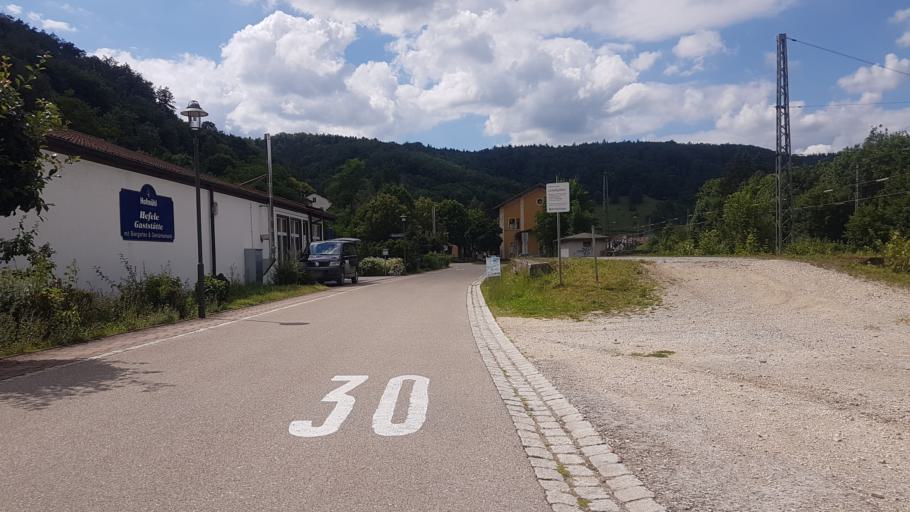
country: DE
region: Bavaria
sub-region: Regierungsbezirk Mittelfranken
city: Solnhofen
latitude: 48.8916
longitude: 10.9960
